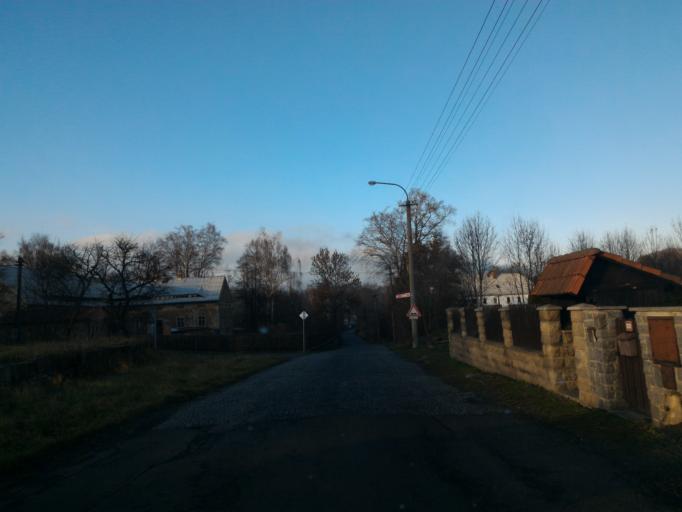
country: CZ
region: Ustecky
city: Varnsdorf
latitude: 50.9157
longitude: 14.6262
